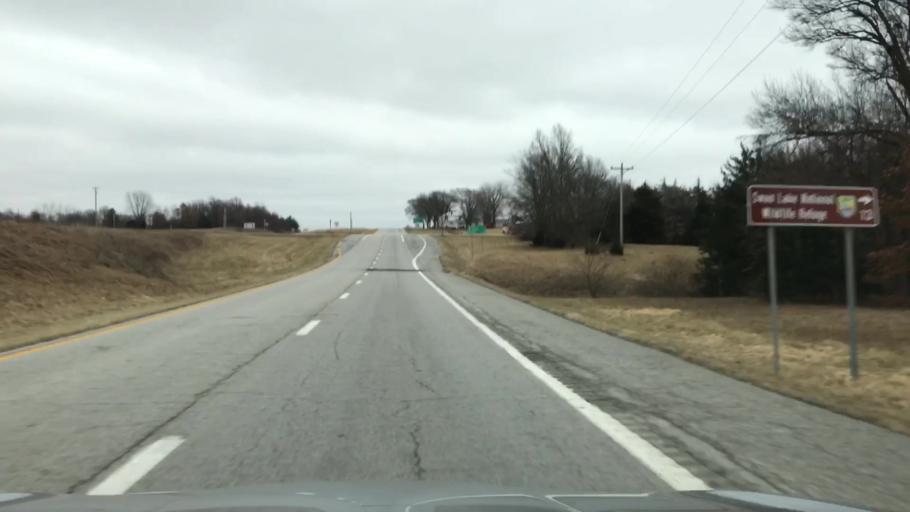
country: US
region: Missouri
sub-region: Linn County
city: Linneus
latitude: 39.7783
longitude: -93.1776
